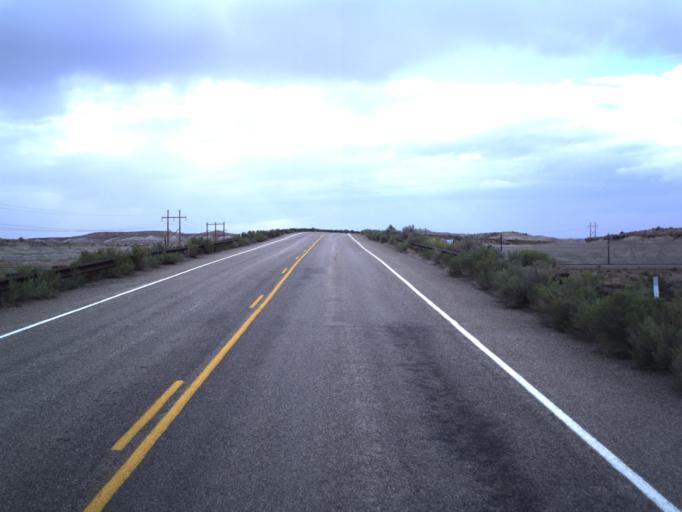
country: US
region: Colorado
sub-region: Rio Blanco County
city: Rangely
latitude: 40.0933
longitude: -109.2253
